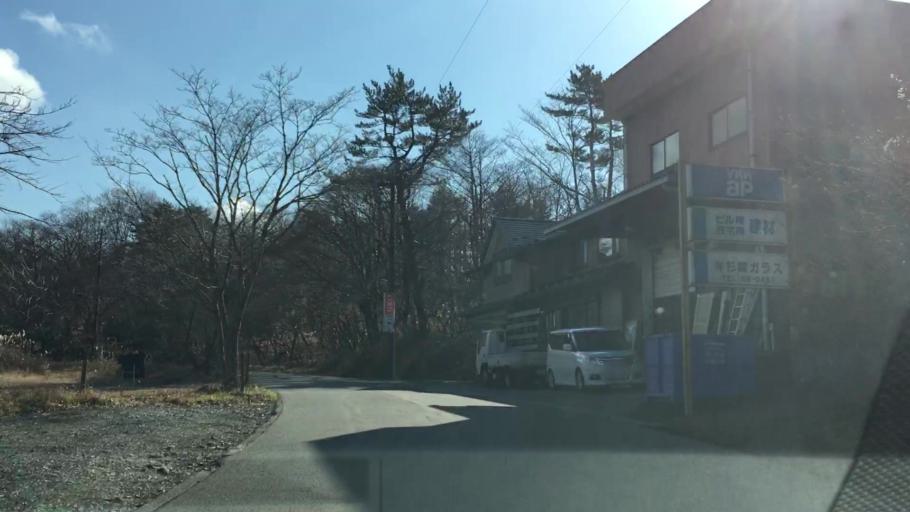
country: JP
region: Shizuoka
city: Gotemba
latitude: 35.3951
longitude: 138.8629
